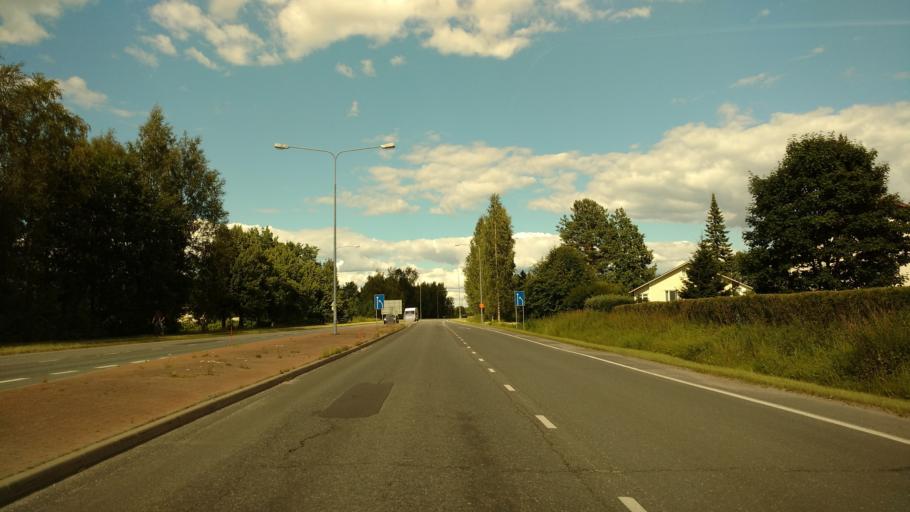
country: FI
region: Varsinais-Suomi
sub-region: Salo
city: Salo
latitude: 60.3927
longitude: 23.1478
